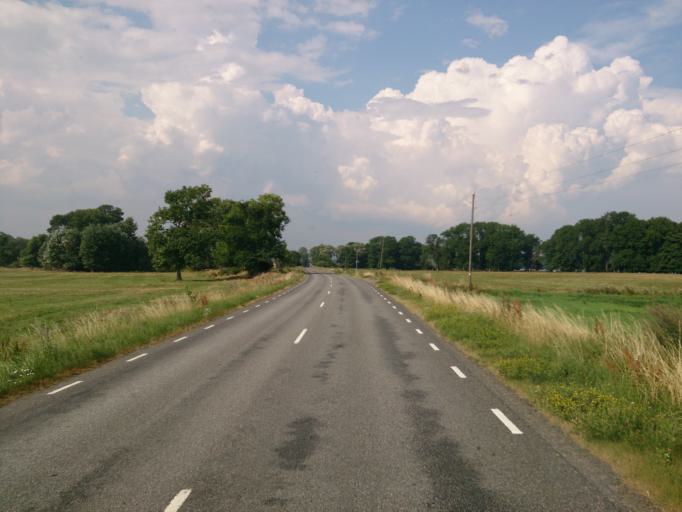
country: SE
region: Skane
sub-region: Kristianstads Kommun
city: Fjalkinge
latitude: 56.0797
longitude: 14.3493
